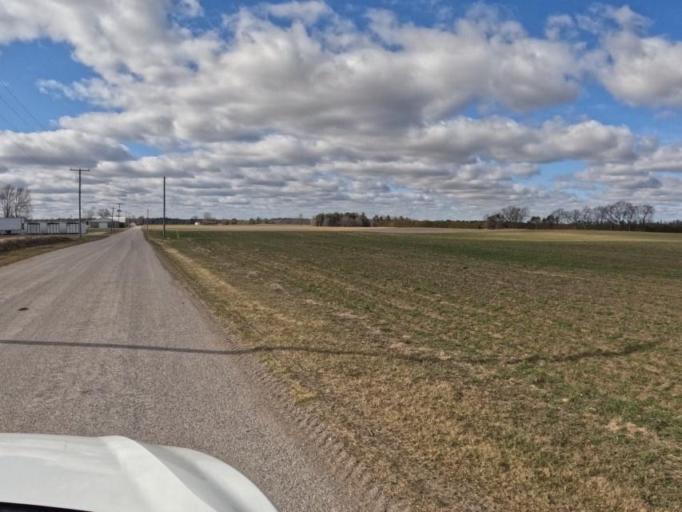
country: CA
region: Ontario
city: Norfolk County
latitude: 42.7438
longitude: -80.3811
